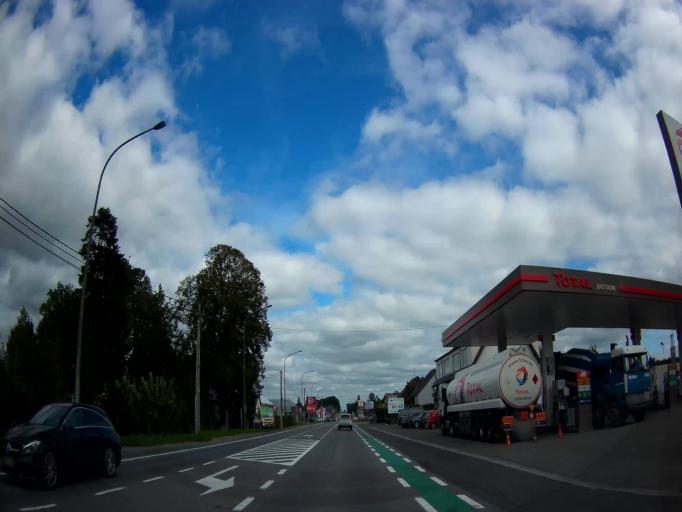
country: BE
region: Wallonia
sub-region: Province du Luxembourg
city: Bastogne
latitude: 50.0024
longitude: 5.6945
